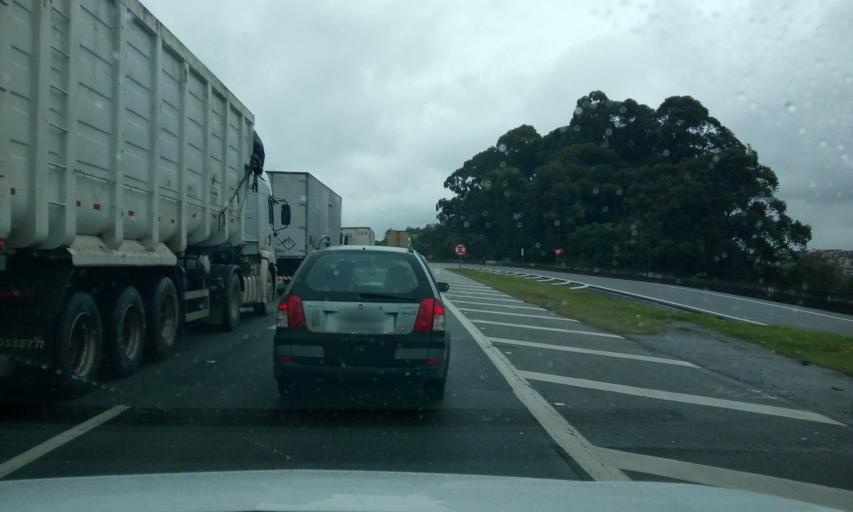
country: BR
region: Sao Paulo
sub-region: Osasco
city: Osasco
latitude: -23.4979
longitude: -46.7295
